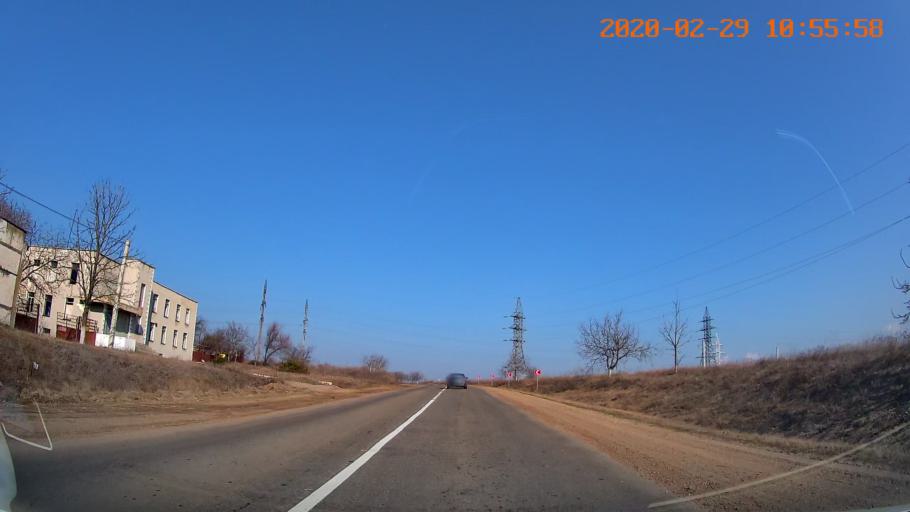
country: MD
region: Telenesti
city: Grigoriopol
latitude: 47.1400
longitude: 29.3257
